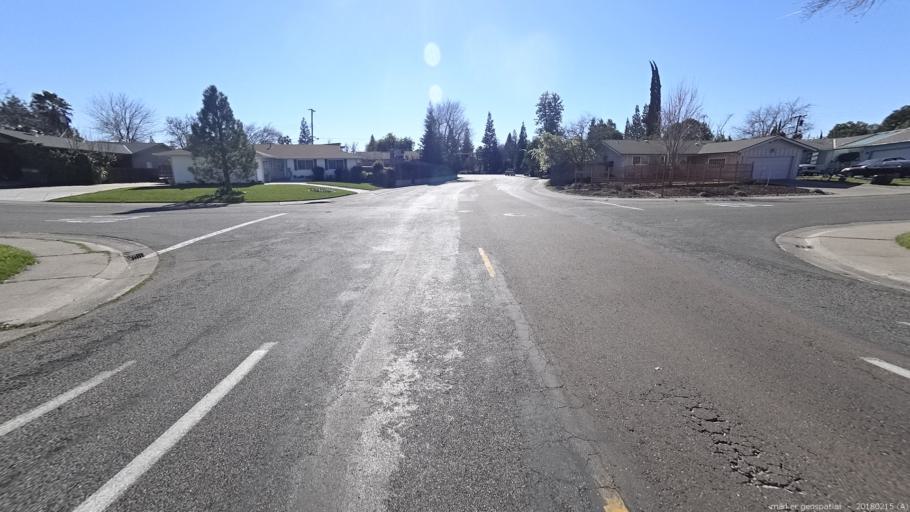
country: US
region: California
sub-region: Sacramento County
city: Foothill Farms
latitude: 38.6645
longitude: -121.3150
